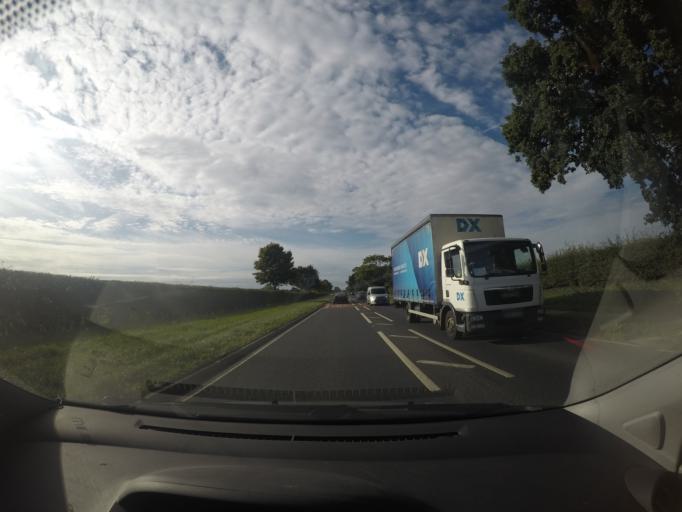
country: GB
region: England
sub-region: City of York
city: Deighton
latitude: 53.8890
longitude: -1.0455
